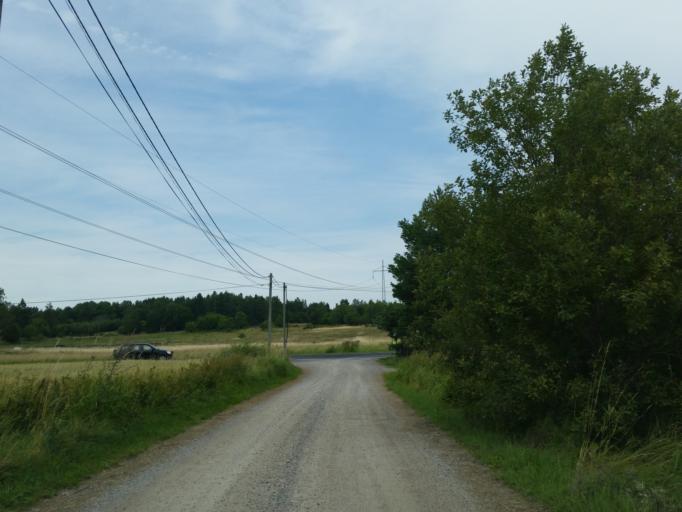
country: SE
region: Soedermanland
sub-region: Strangnas Kommun
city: Akers Styckebruk
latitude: 59.2724
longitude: 17.1364
